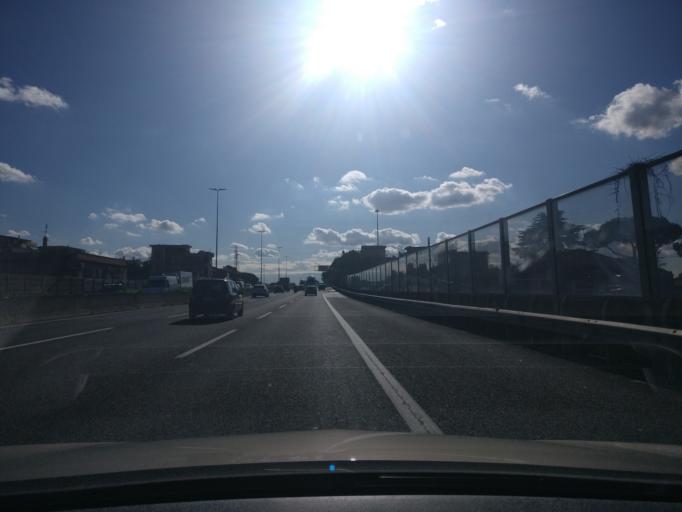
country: IT
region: Latium
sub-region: Citta metropolitana di Roma Capitale
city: Ciampino
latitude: 41.8434
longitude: 12.5933
